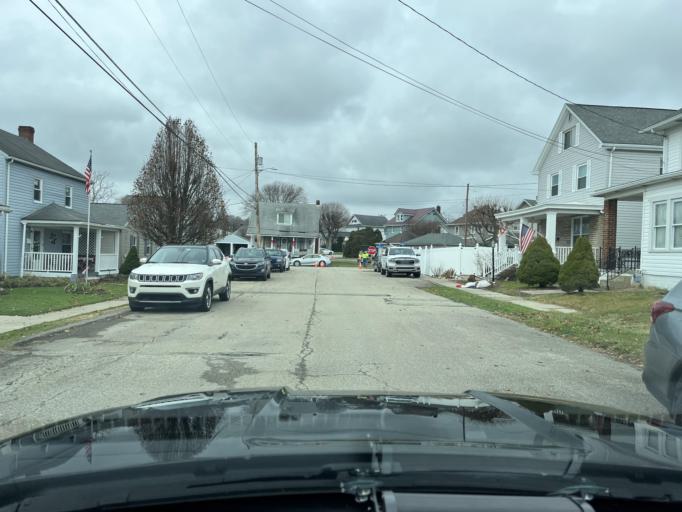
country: US
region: Pennsylvania
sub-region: Fayette County
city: South Uniontown
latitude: 39.8945
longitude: -79.7461
